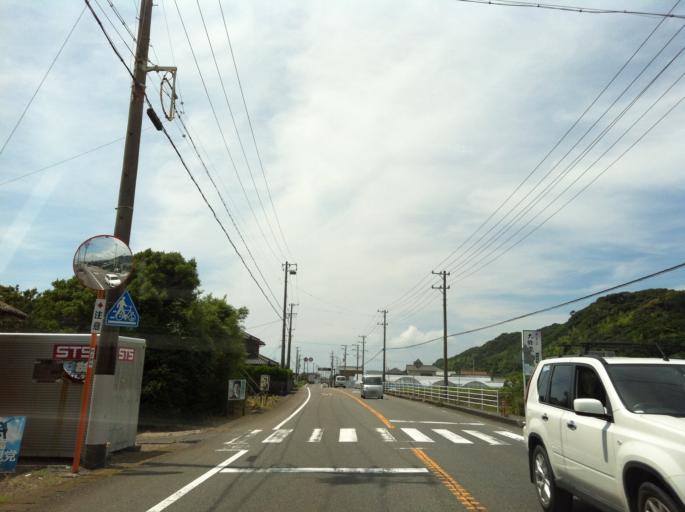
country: JP
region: Shizuoka
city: Sagara
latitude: 34.7099
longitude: 138.2134
